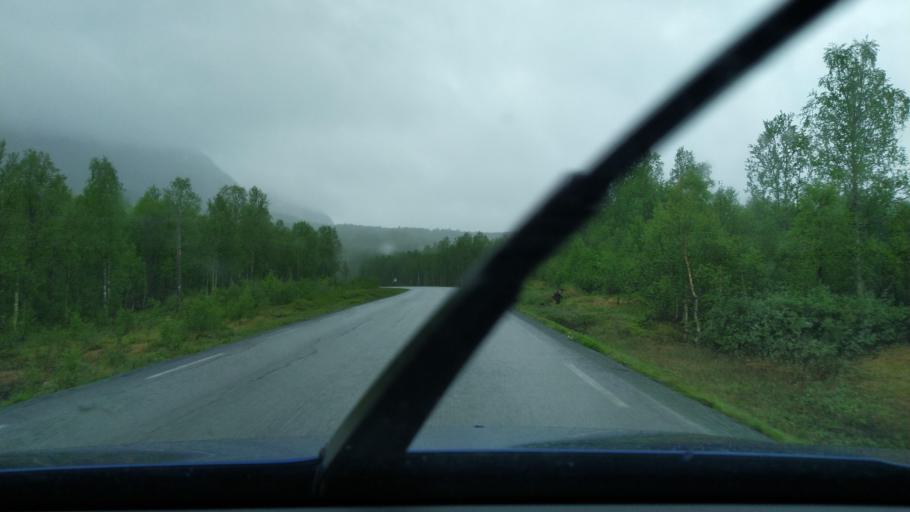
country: NO
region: Troms
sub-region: Dyroy
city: Brostadbotn
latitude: 69.0232
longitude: 17.7374
